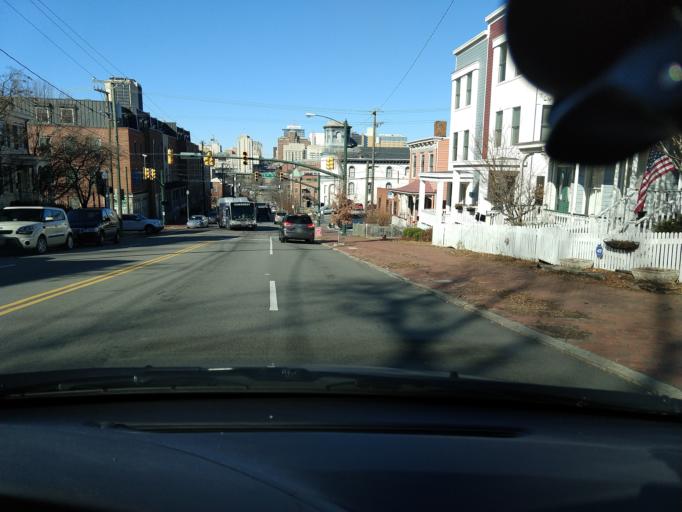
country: US
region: Virginia
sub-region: City of Richmond
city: Richmond
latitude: 37.5336
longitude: -77.4220
